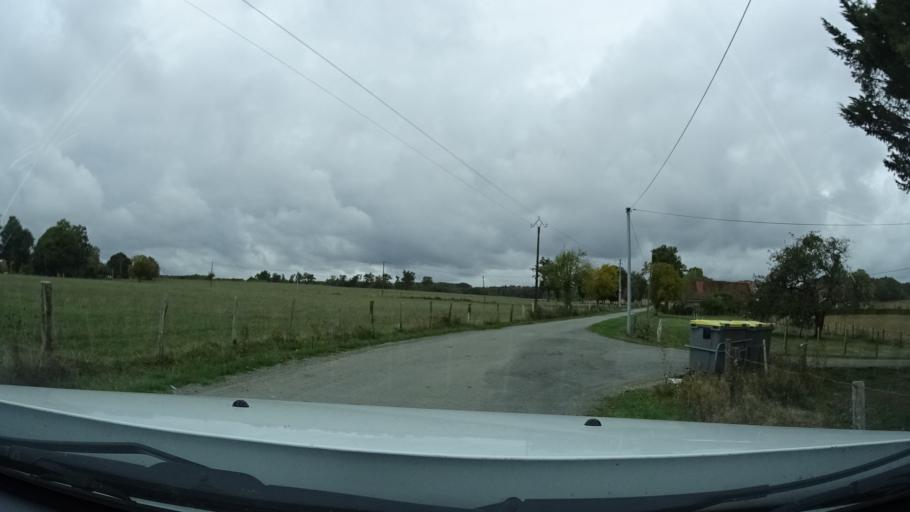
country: FR
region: Aquitaine
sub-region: Departement de la Dordogne
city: La Coquille
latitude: 45.5219
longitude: 0.9323
